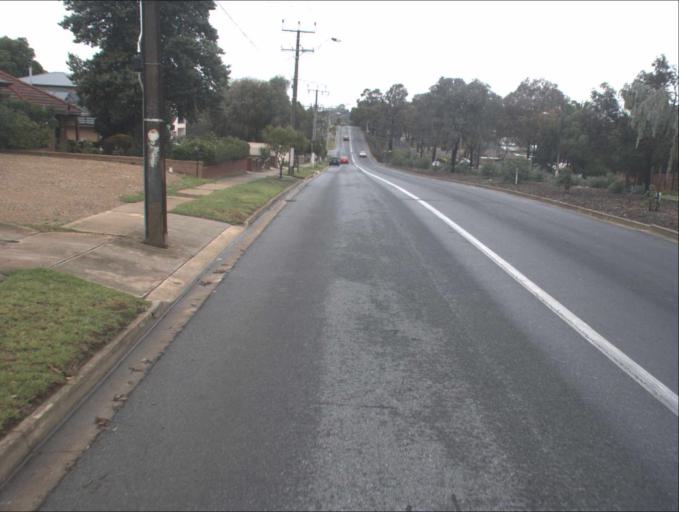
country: AU
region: South Australia
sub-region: Port Adelaide Enfield
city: Gilles Plains
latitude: -34.8373
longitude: 138.6625
